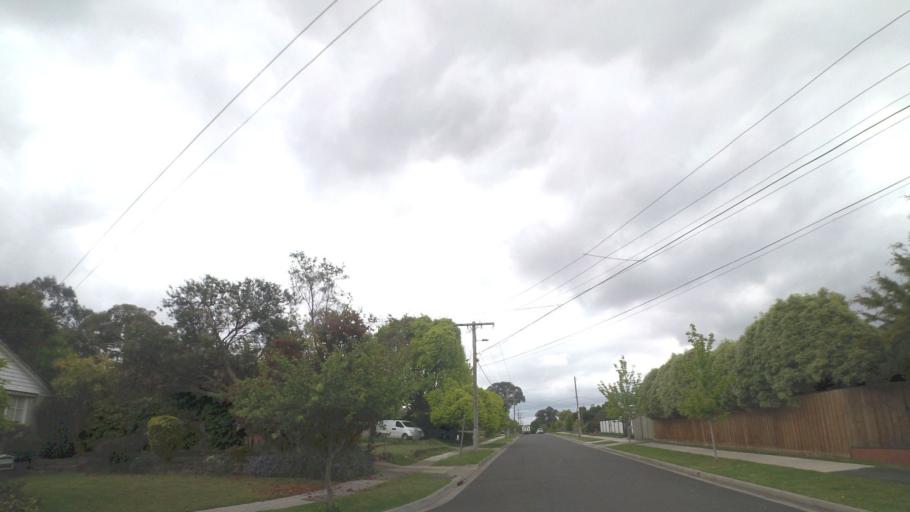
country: AU
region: Victoria
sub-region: Maroondah
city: Heathmont
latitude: -37.8460
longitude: 145.2520
